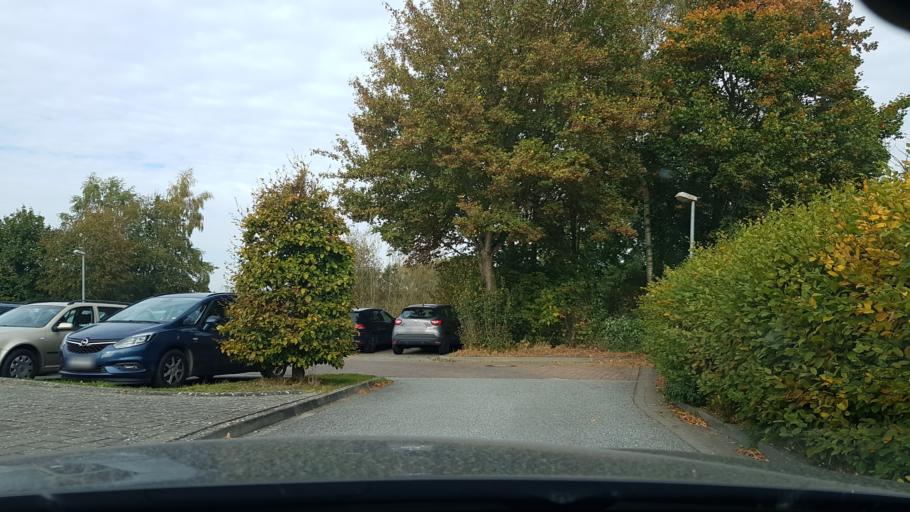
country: DE
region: Lower Saxony
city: Beverstedt
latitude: 53.4352
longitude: 8.8157
